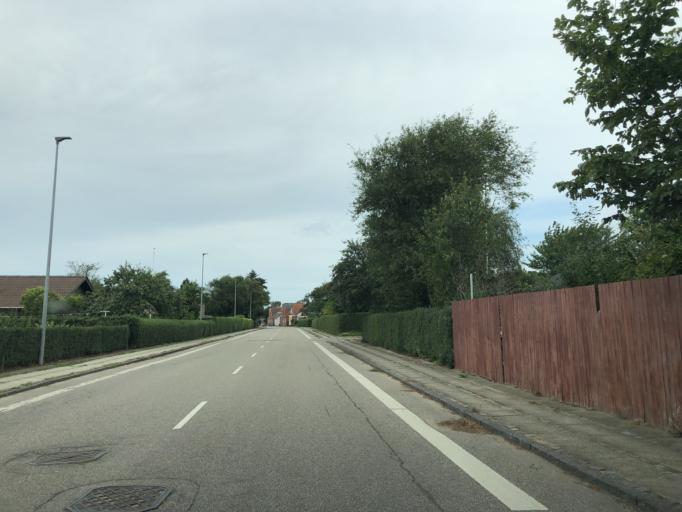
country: DK
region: Central Jutland
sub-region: Ringkobing-Skjern Kommune
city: Ringkobing
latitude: 56.0966
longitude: 8.2566
